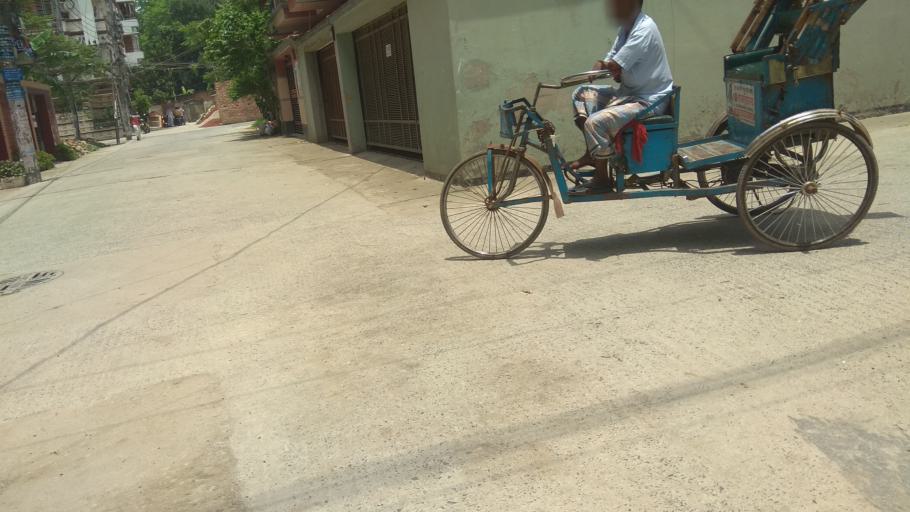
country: BD
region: Dhaka
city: Tungi
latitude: 23.8186
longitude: 90.3574
